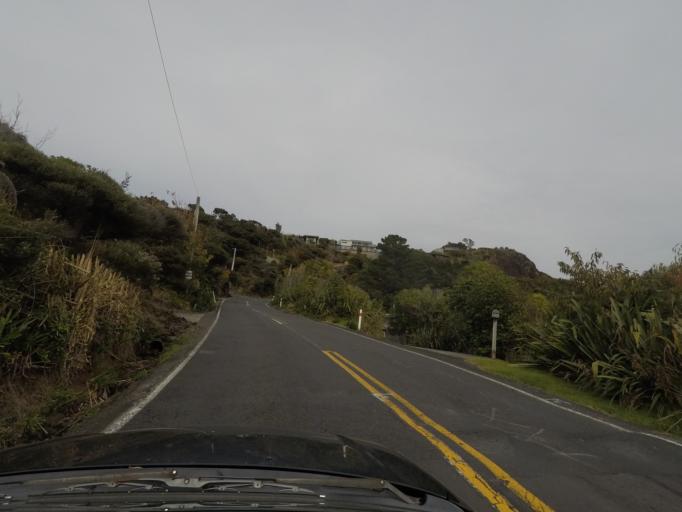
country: NZ
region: Auckland
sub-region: Auckland
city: Muriwai Beach
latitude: -36.9612
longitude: 174.4750
